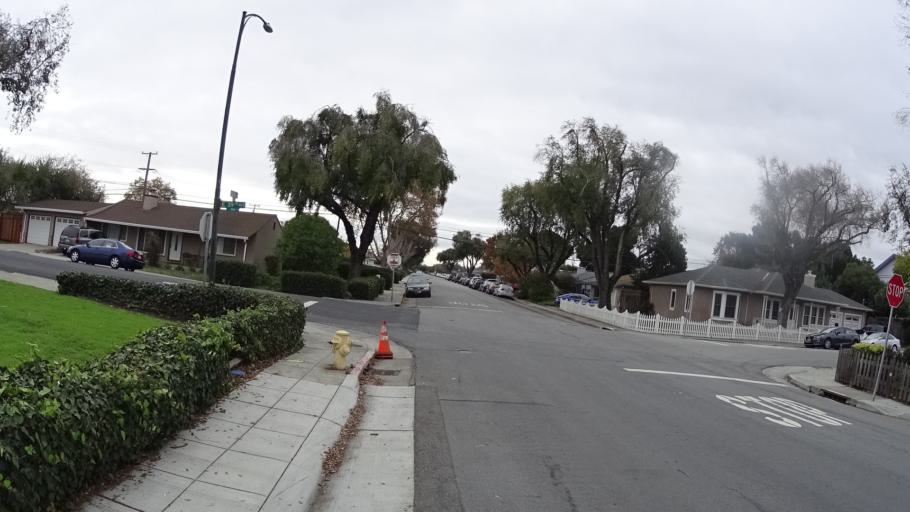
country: US
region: California
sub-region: San Mateo County
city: Belmont
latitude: 37.5375
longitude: -122.2855
